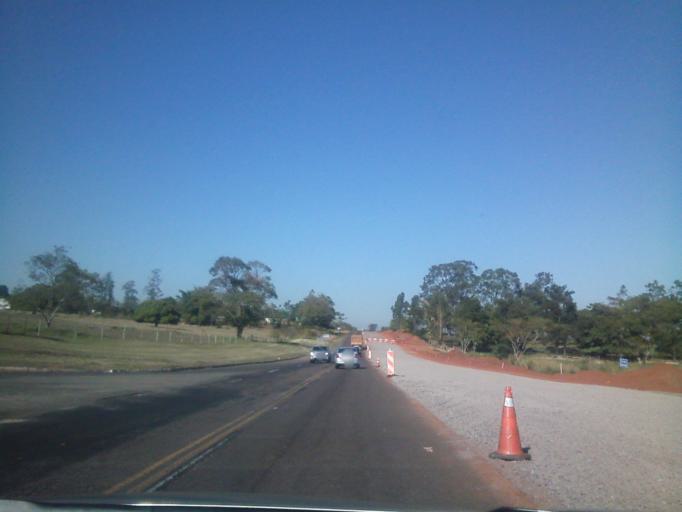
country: BR
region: Sao Paulo
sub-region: Pirapozinho
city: Pirapozinho
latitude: -22.2332
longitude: -51.4437
